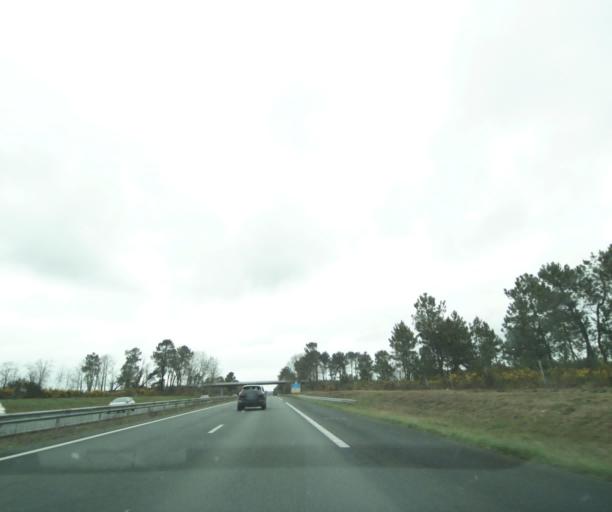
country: FR
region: Aquitaine
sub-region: Departement de la Gironde
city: Saint-Savin
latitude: 45.1737
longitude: -0.4842
